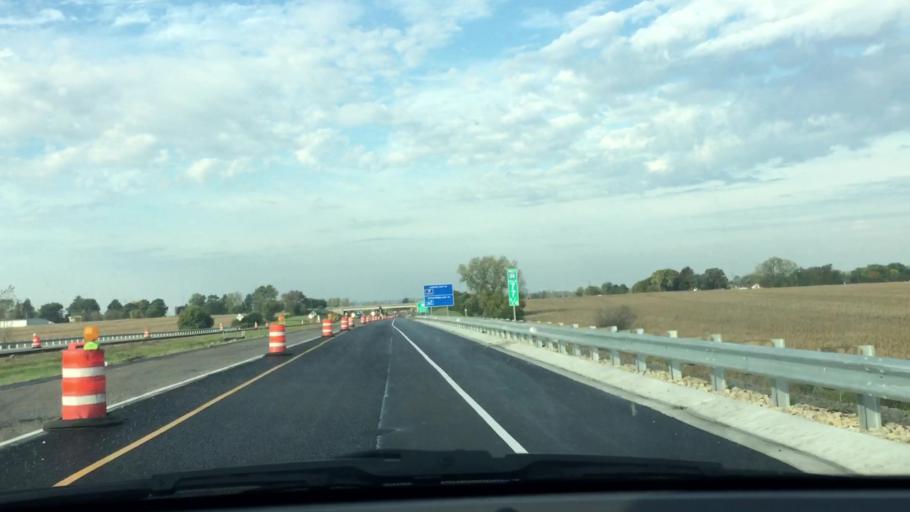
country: US
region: Illinois
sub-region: Ogle County
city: Rochelle
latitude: 41.9018
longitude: -89.0466
